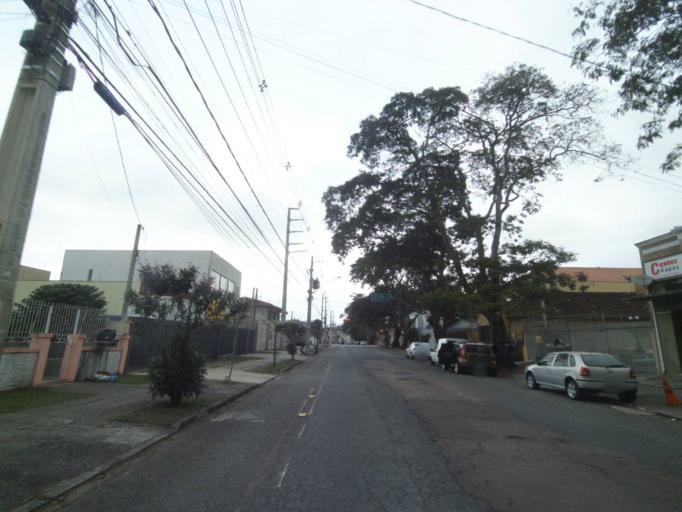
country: BR
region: Parana
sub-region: Curitiba
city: Curitiba
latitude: -25.4457
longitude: -49.2554
